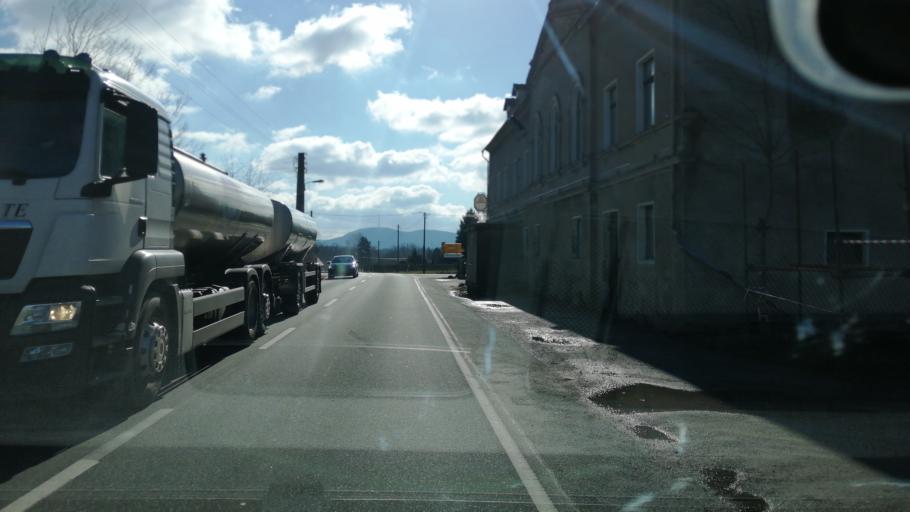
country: DE
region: Saxony
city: Lobau
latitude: 51.1507
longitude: 14.7180
